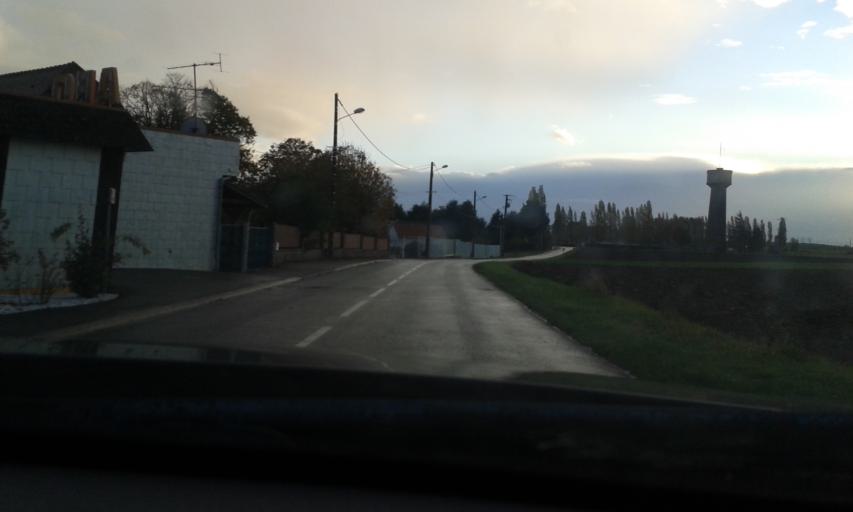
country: FR
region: Centre
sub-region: Departement du Loiret
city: Gidy
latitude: 47.9960
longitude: 1.8396
